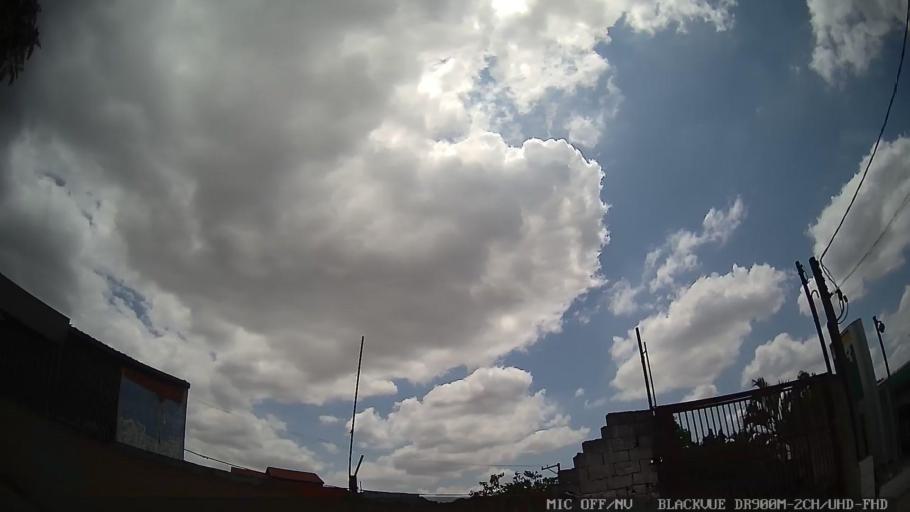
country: BR
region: Sao Paulo
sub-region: Ferraz De Vasconcelos
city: Ferraz de Vasconcelos
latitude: -23.5328
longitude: -46.4626
